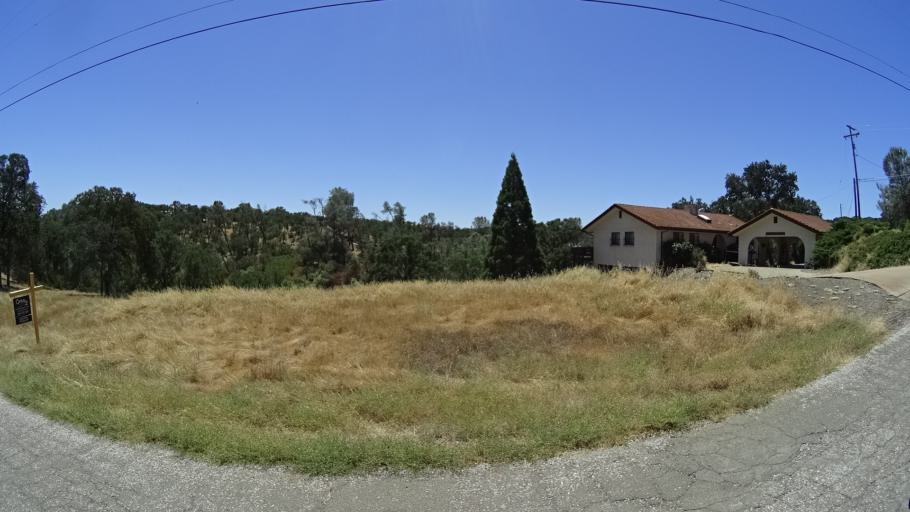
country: US
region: California
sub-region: Calaveras County
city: Rancho Calaveras
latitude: 38.1514
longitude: -120.8355
